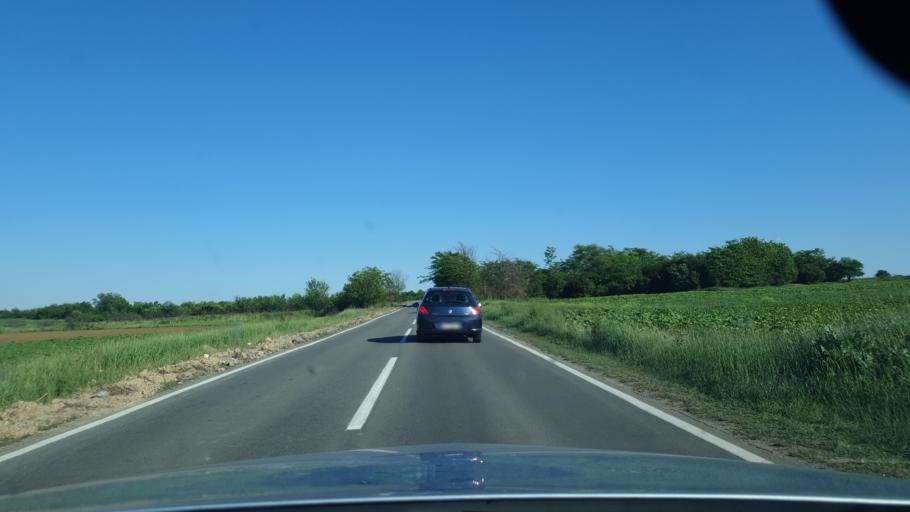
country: RS
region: Central Serbia
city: Sremcica
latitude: 44.7058
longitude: 20.3707
